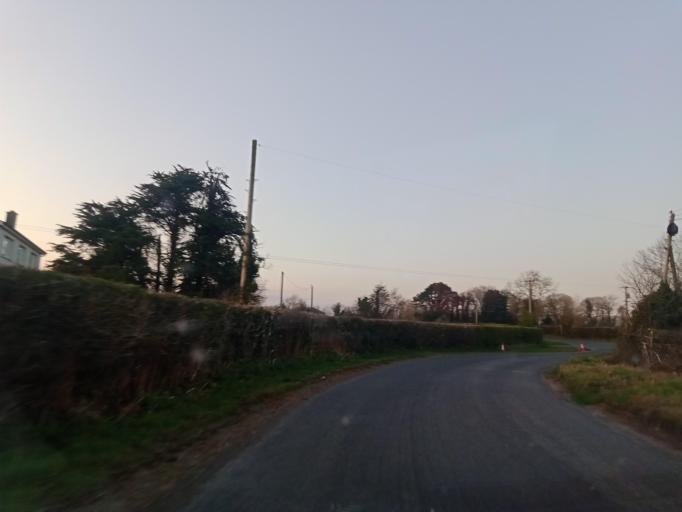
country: IE
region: Leinster
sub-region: Laois
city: Abbeyleix
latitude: 52.9547
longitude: -7.3615
